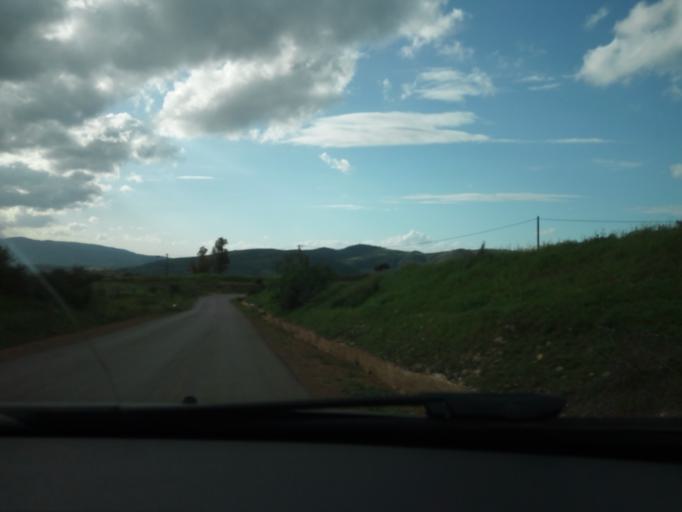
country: DZ
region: Tipaza
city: El Affroun
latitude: 36.3724
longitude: 2.5096
